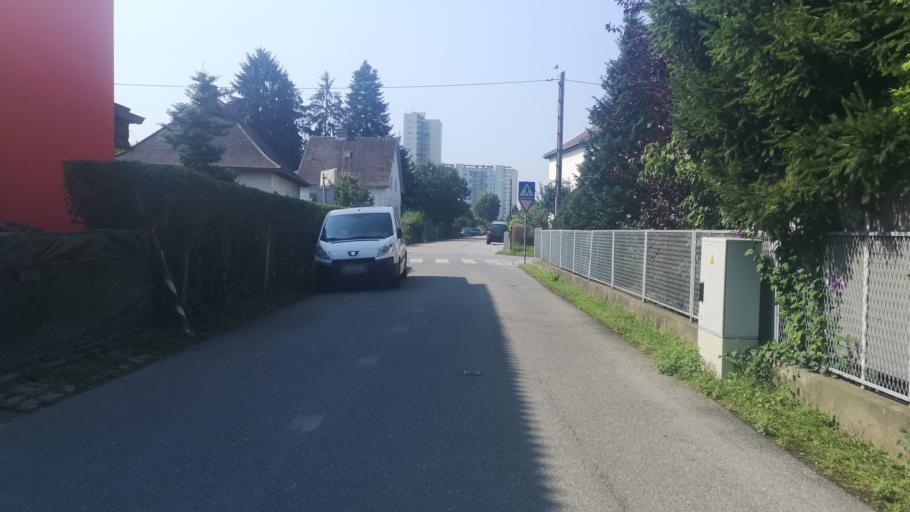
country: AT
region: Styria
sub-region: Graz Stadt
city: Wetzelsdorf
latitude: 47.0438
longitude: 15.4131
